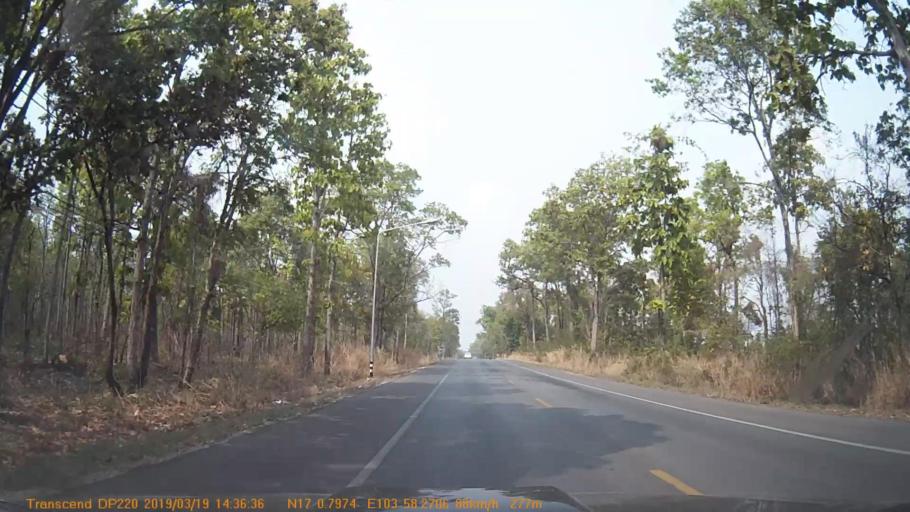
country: TH
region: Sakon Nakhon
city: Phu Phan
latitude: 17.0136
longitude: 103.9713
